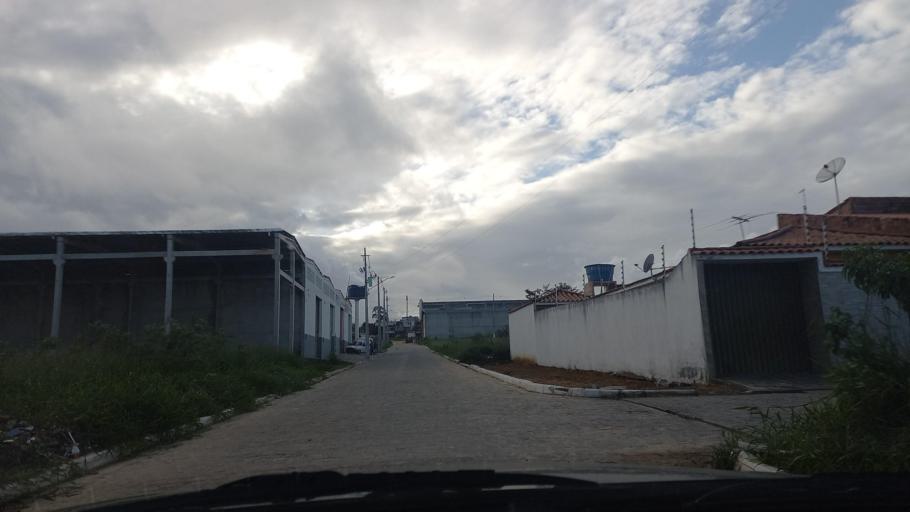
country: BR
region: Pernambuco
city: Garanhuns
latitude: -8.9097
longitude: -36.4862
